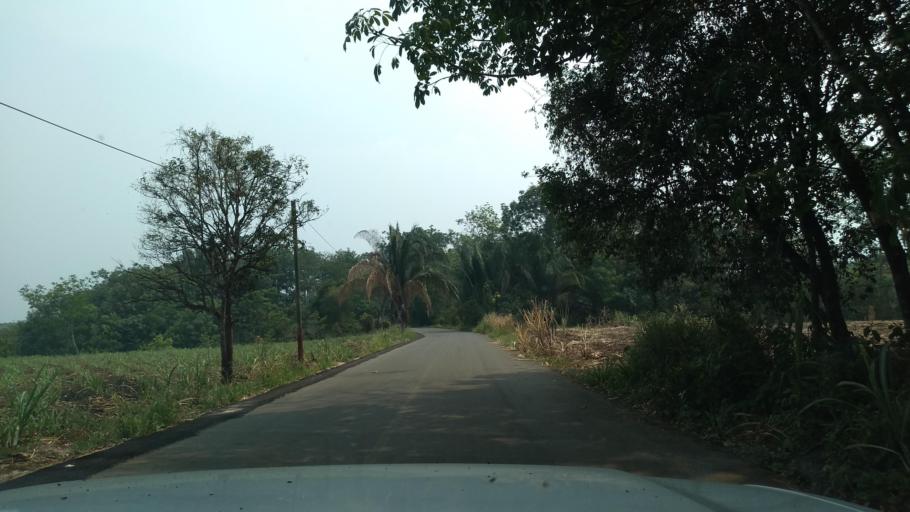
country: MX
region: Veracruz
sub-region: Tezonapa
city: Laguna Chica (Pueblo Nuevo)
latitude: 18.5347
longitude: -96.7867
